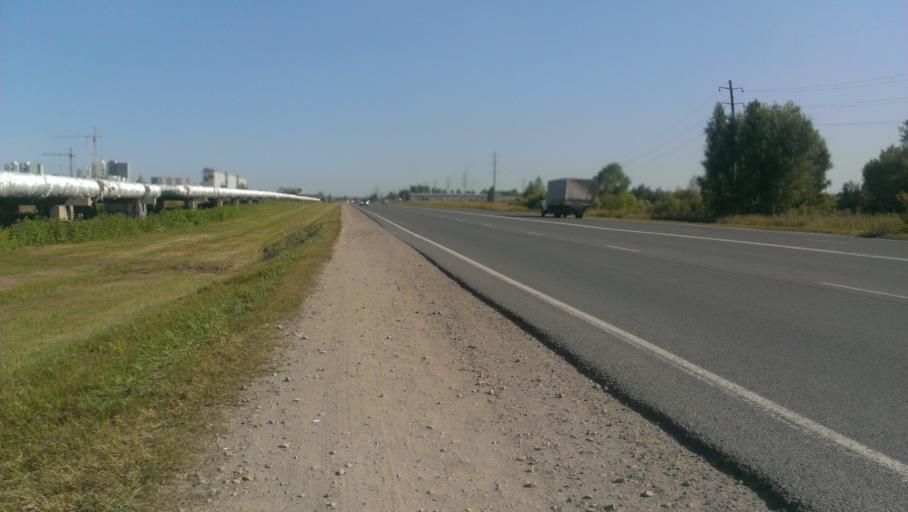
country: RU
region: Altai Krai
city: Novosilikatnyy
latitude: 53.3450
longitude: 83.6346
